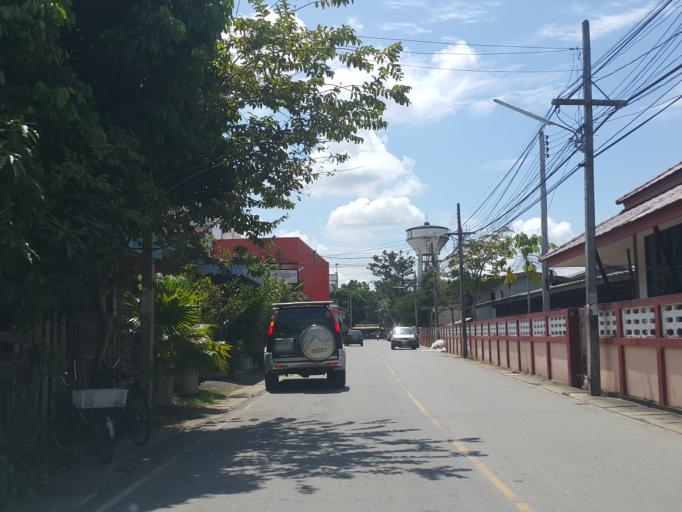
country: TH
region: Chiang Mai
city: Phrao
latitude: 19.3668
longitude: 99.2028
